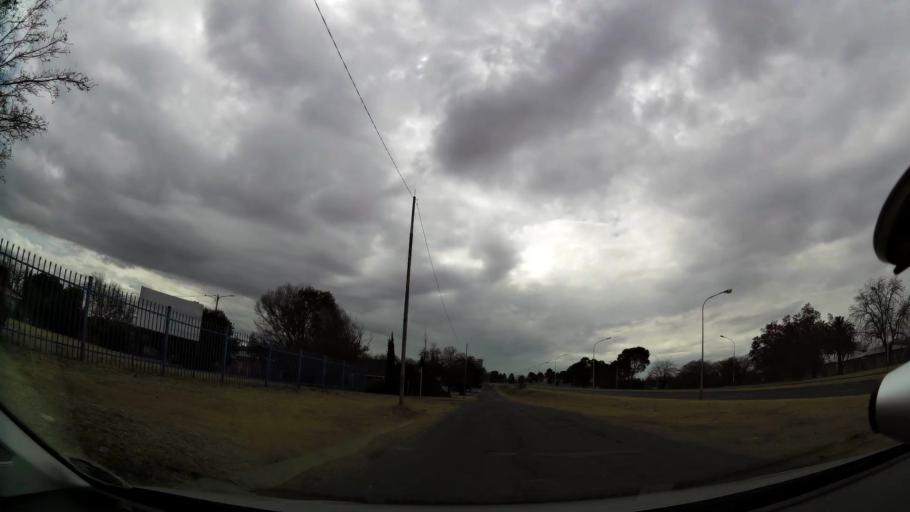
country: ZA
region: Orange Free State
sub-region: Fezile Dabi District Municipality
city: Kroonstad
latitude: -27.6425
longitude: 27.2328
